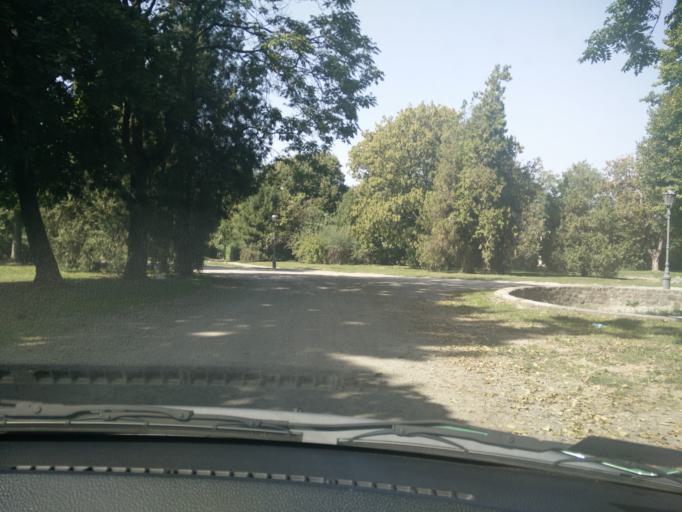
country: RS
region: Autonomna Pokrajina Vojvodina
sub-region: Juznobacki Okrug
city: Petrovaradin
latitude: 45.2492
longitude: 19.8673
